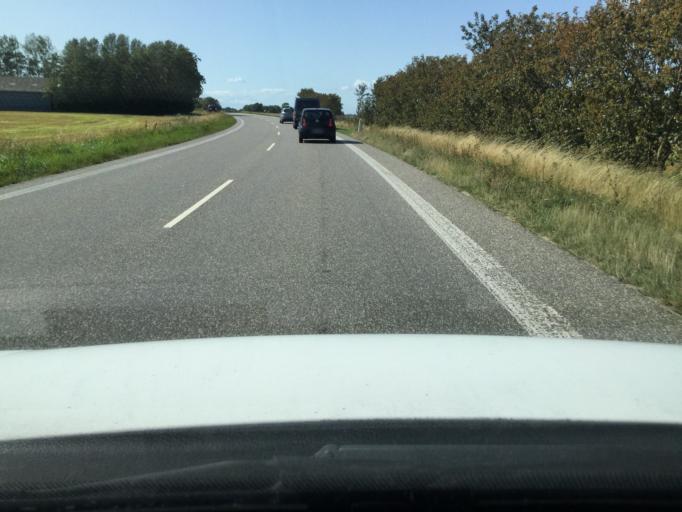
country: DK
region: Zealand
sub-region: Lolland Kommune
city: Nakskov
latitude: 54.8090
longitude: 11.2205
